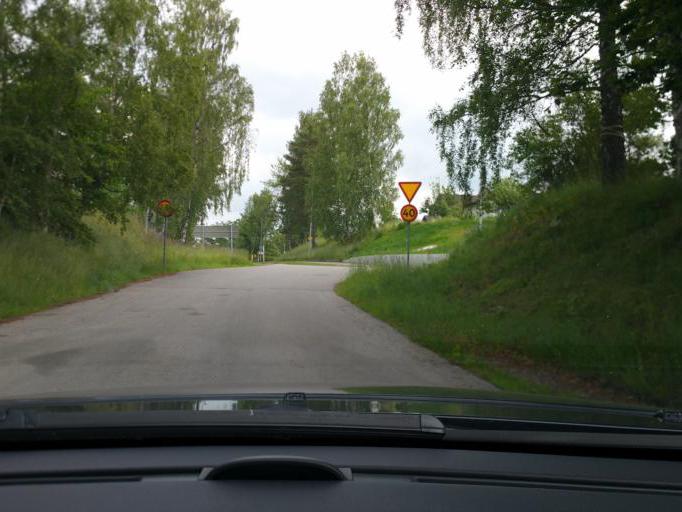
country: SE
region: Kronoberg
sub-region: Vaxjo Kommun
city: Lammhult
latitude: 57.1745
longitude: 14.5861
